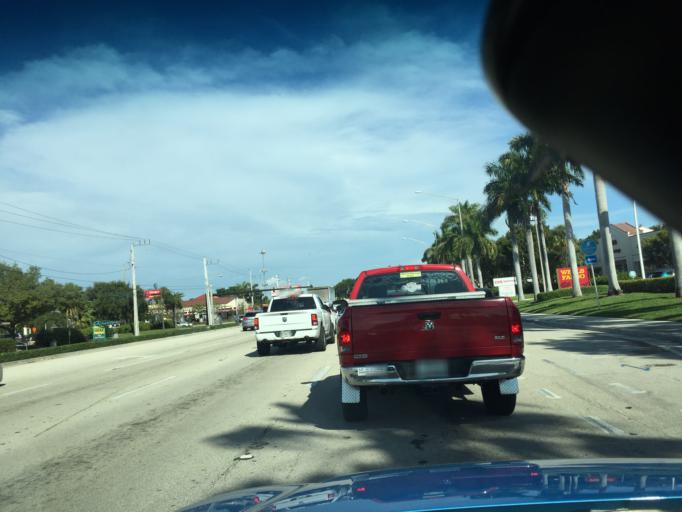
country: US
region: Florida
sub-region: Broward County
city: Lighthouse Point
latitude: 26.2740
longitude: -80.0971
